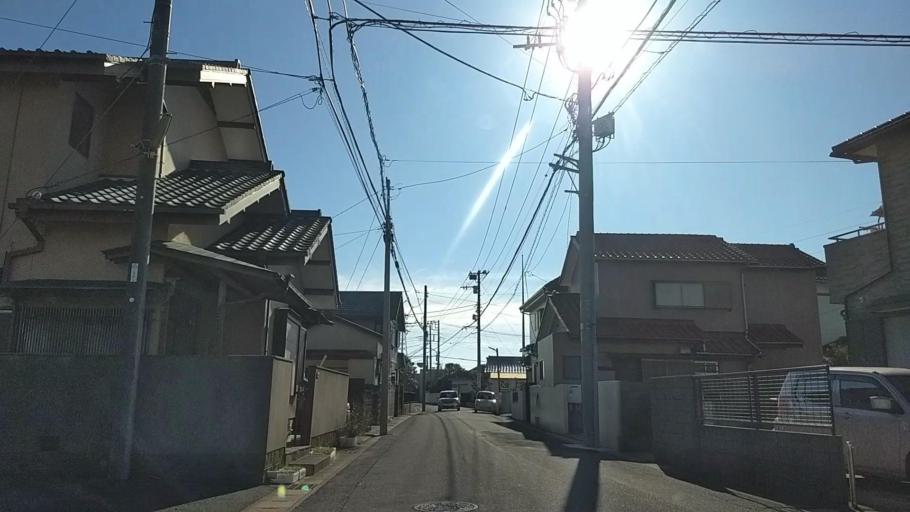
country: JP
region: Chiba
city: Hasaki
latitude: 35.7236
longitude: 140.8420
